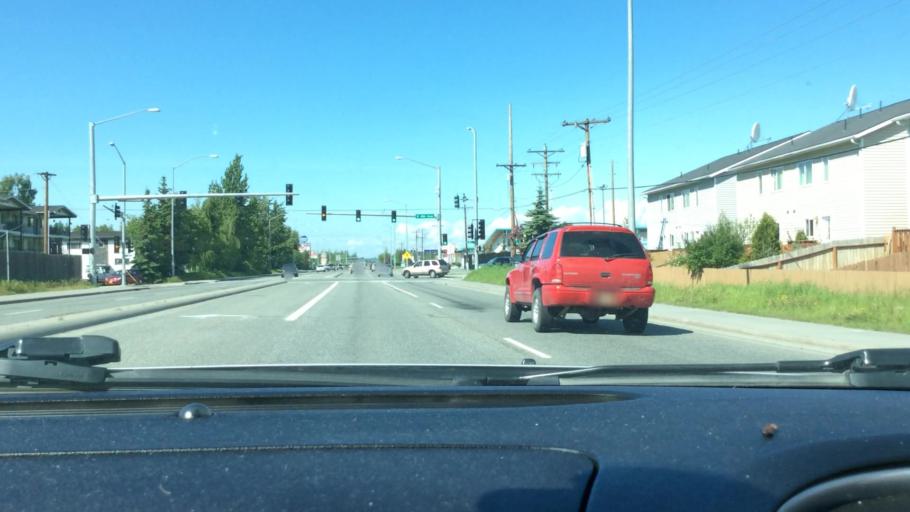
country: US
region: Alaska
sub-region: Anchorage Municipality
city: Anchorage
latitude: 61.2180
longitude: -149.7784
